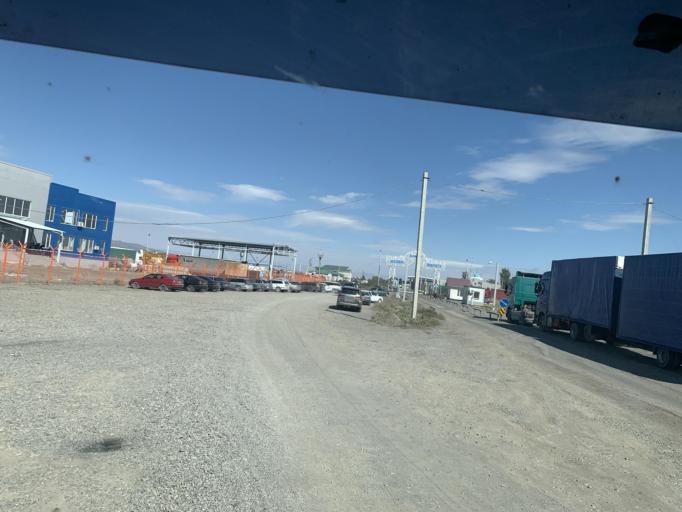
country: CN
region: Xinjiang Uygur Zizhiqu
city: Tacheng
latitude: 46.6772
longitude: 82.7738
